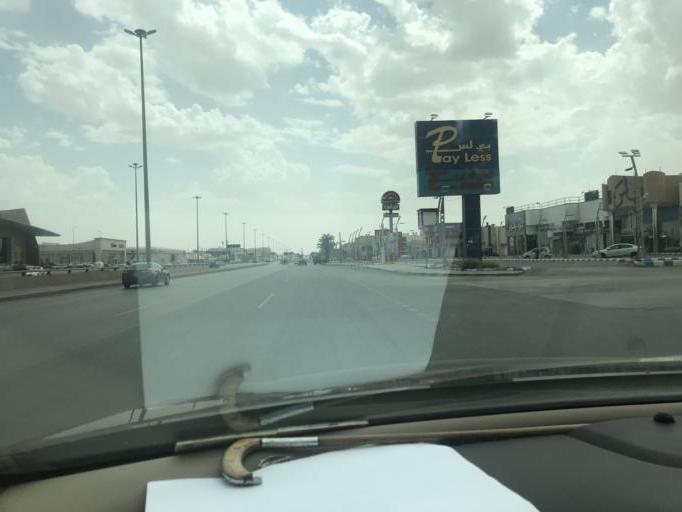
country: SA
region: Ar Riyad
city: Riyadh
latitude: 24.7294
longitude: 46.7852
